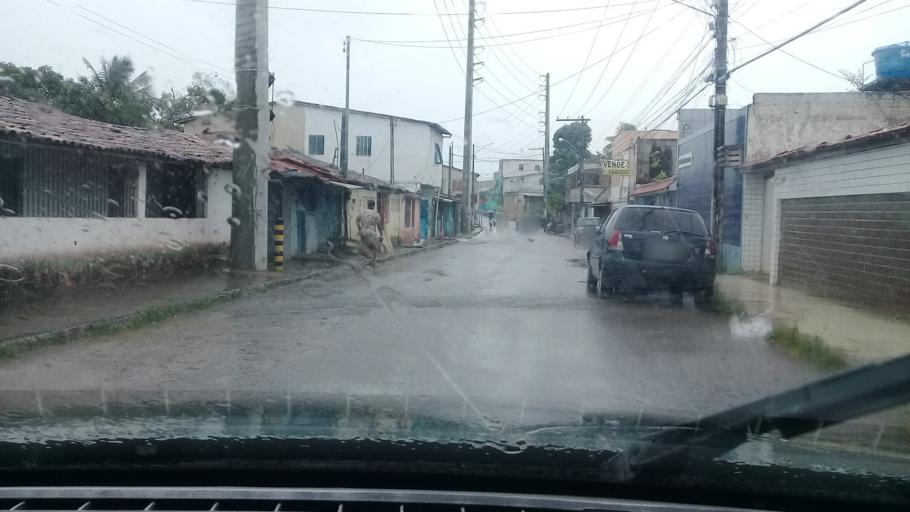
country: BR
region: Pernambuco
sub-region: Paulista
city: Paulista
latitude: -7.9618
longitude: -34.8901
